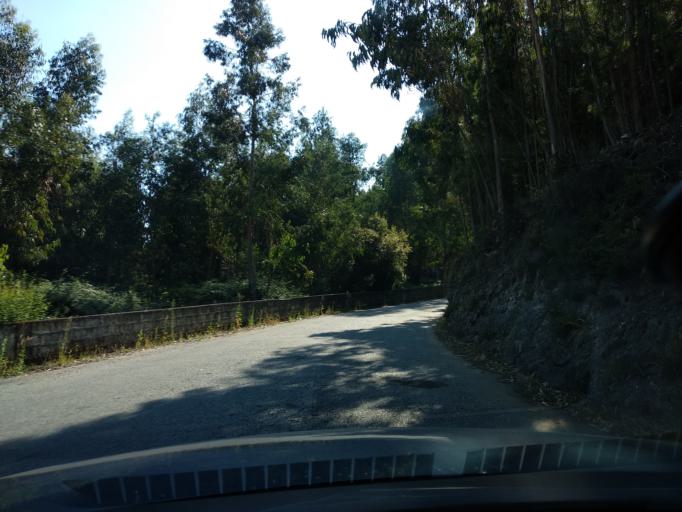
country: PT
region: Porto
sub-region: Paredes
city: Madalena
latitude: 41.2186
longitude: -8.3662
